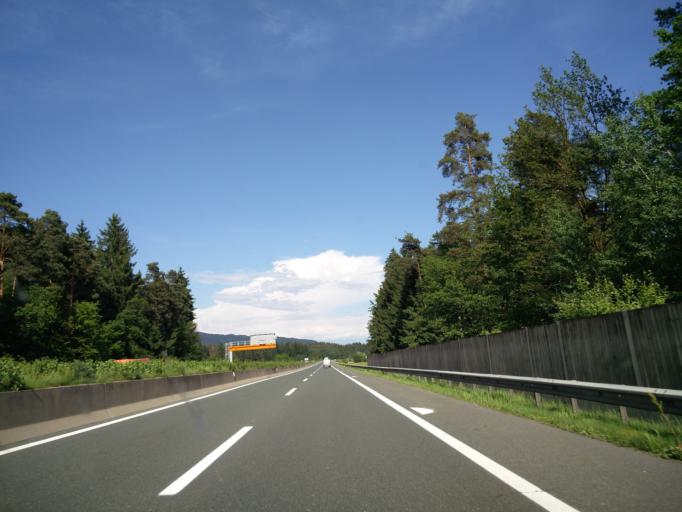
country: AT
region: Carinthia
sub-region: Politischer Bezirk Klagenfurt Land
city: Poggersdorf
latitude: 46.6429
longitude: 14.4846
